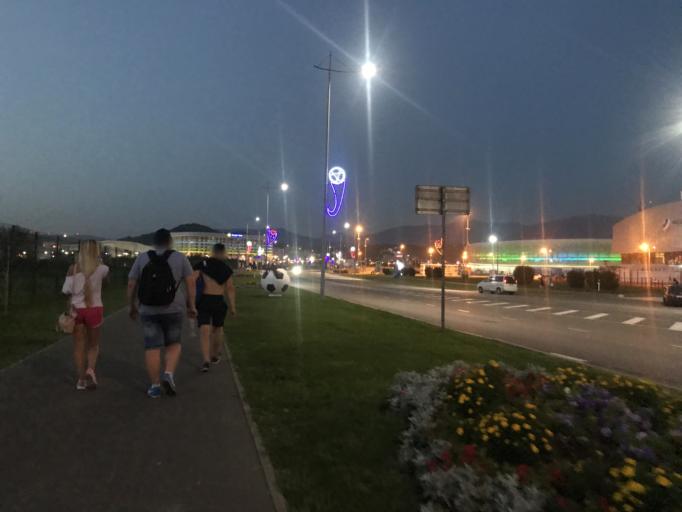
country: RU
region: Krasnodarskiy
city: Adler
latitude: 43.4065
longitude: 39.9473
